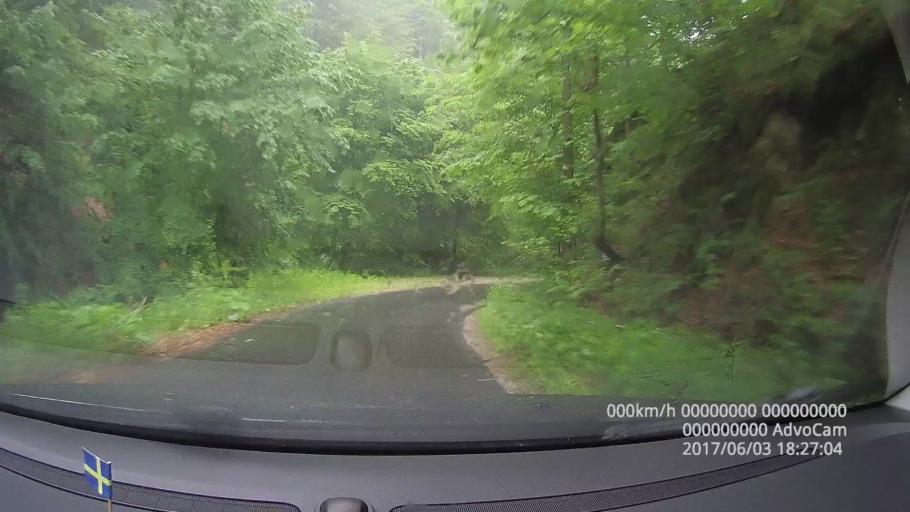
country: RO
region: Gorj
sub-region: Comuna Runcu
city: Dobrita
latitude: 45.1650
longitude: 23.1932
